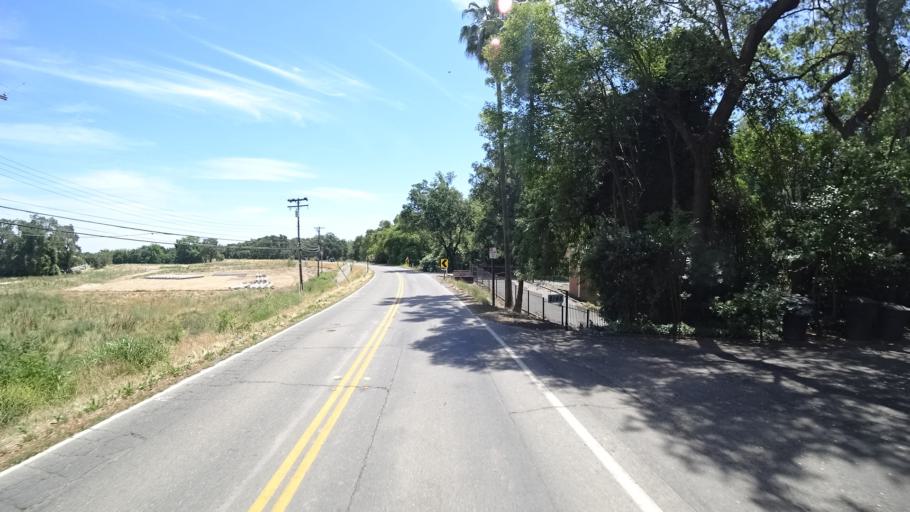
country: US
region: California
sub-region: Yolo County
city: West Sacramento
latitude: 38.5991
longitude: -121.5464
